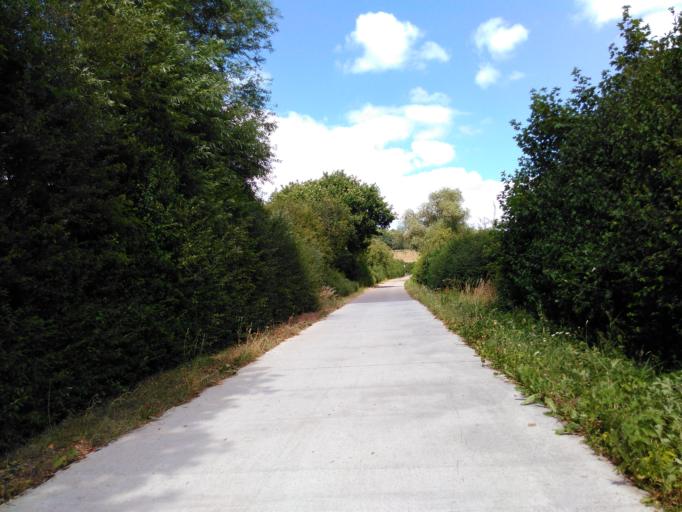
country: LU
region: Luxembourg
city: Hautcharage
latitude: 49.5762
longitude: 5.8958
